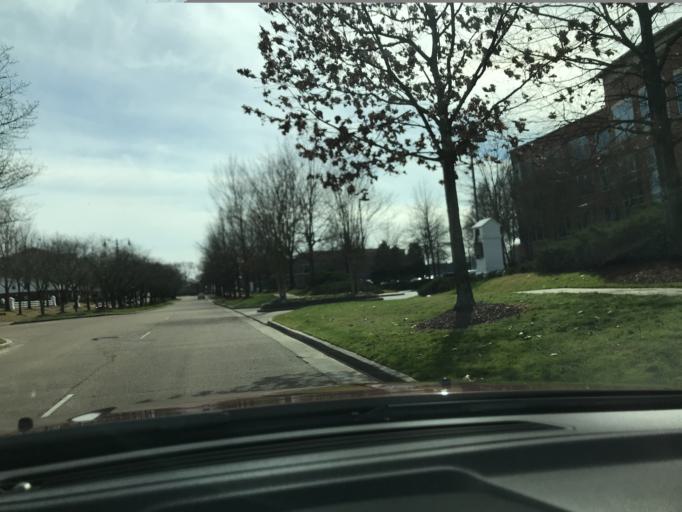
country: US
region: Tennessee
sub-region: Shelby County
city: Collierville
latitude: 35.0406
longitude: -89.7033
